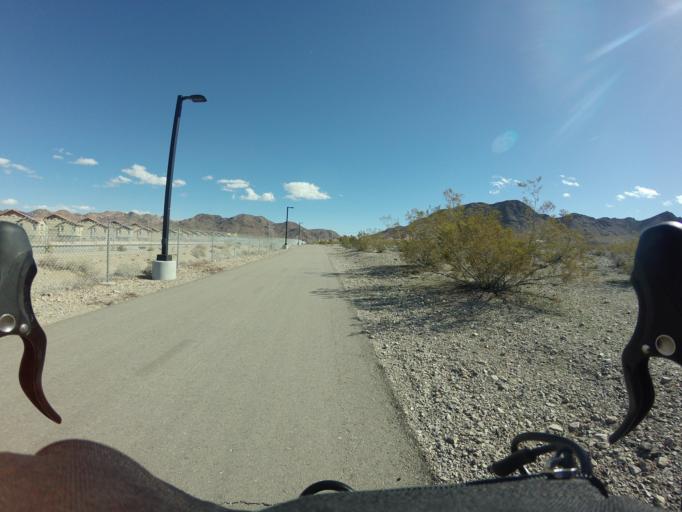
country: US
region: Nevada
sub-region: Clark County
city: Henderson
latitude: 35.9861
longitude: -114.9330
